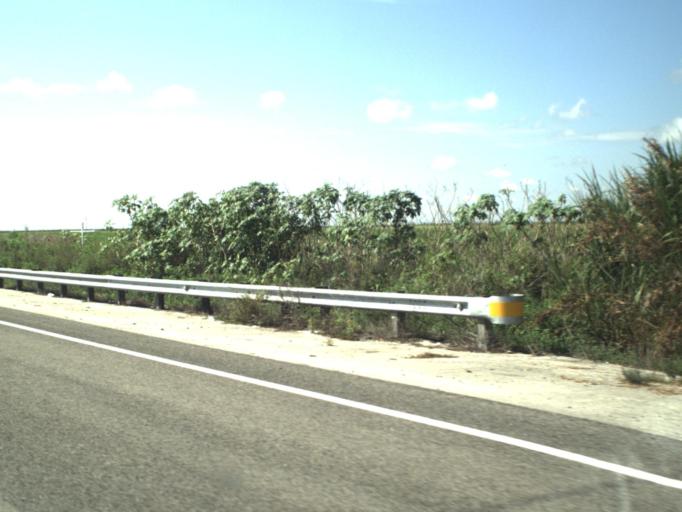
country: US
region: Florida
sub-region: Palm Beach County
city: Belle Glade Camp
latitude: 26.3712
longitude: -80.5661
